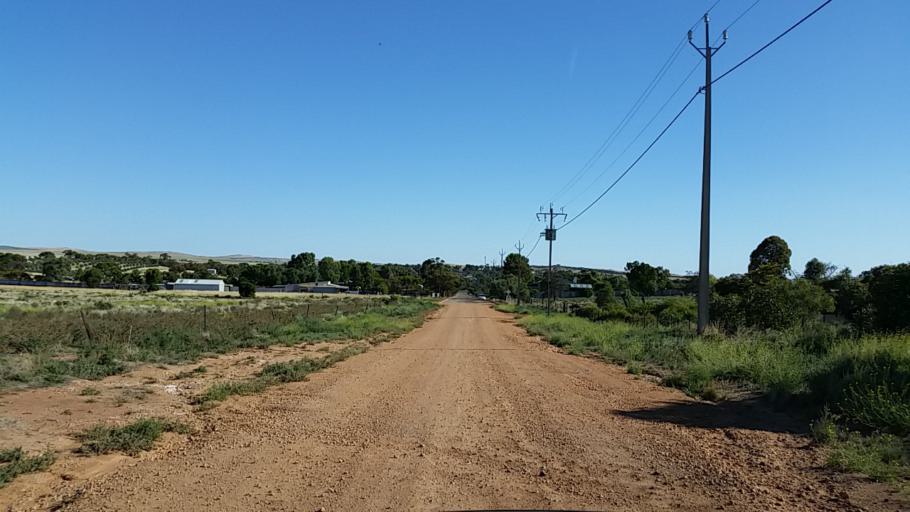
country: AU
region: South Australia
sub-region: Peterborough
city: Peterborough
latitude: -32.9642
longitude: 138.8317
